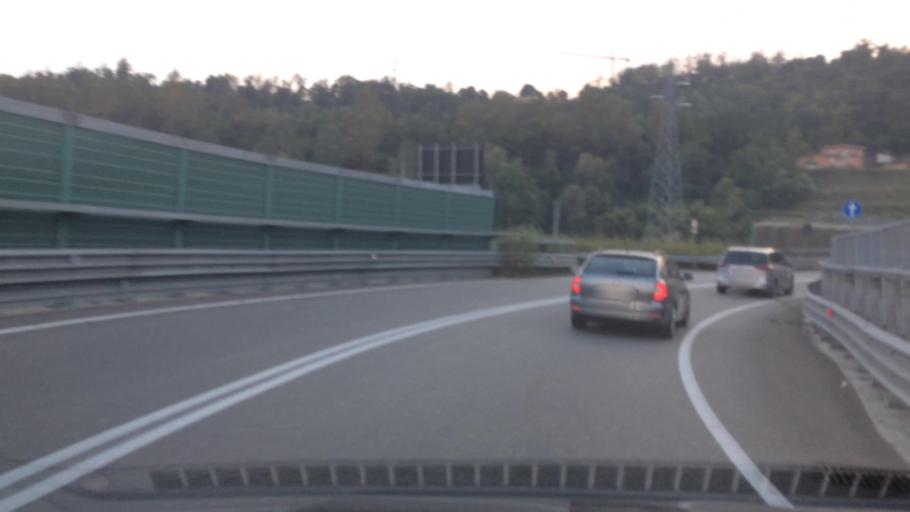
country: IT
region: Lombardy
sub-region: Provincia di Como
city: Casnate Con Bernate
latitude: 45.7720
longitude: 9.0763
